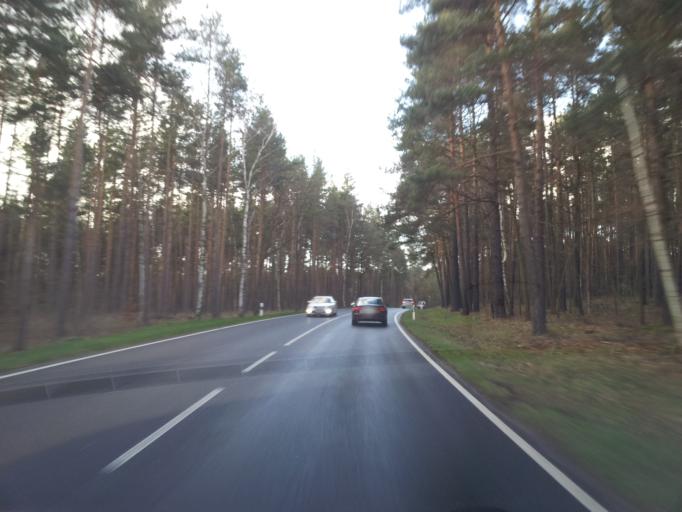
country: DE
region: Saxony
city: Konigsbruck
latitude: 51.2740
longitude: 13.9077
